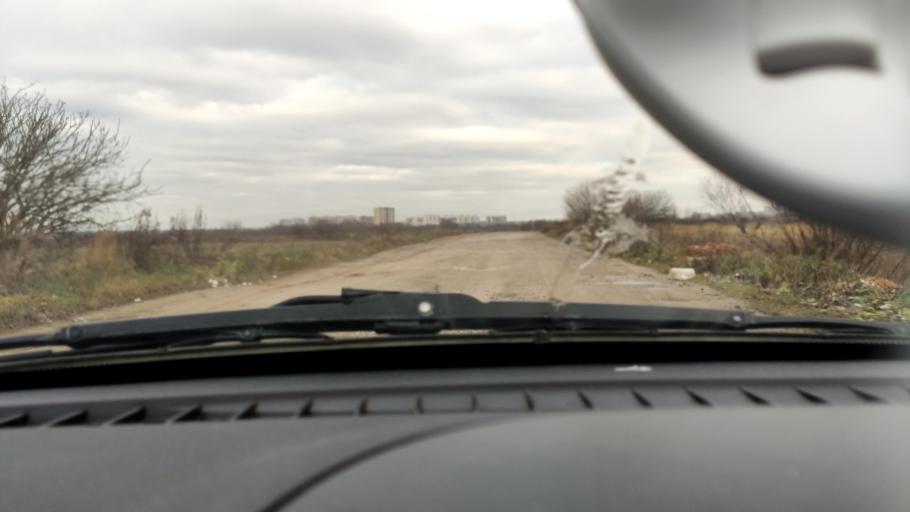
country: RU
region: Perm
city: Kondratovo
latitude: 57.9897
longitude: 56.0916
